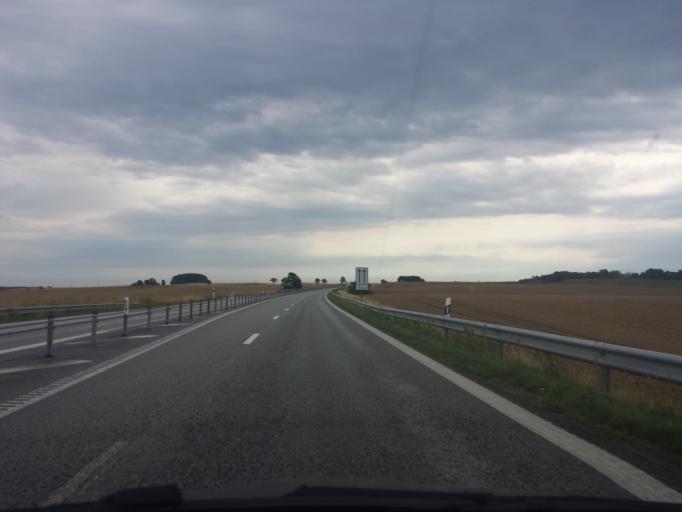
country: SE
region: Skane
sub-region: Skurups Kommun
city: Rydsgard
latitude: 55.4719
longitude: 13.6925
